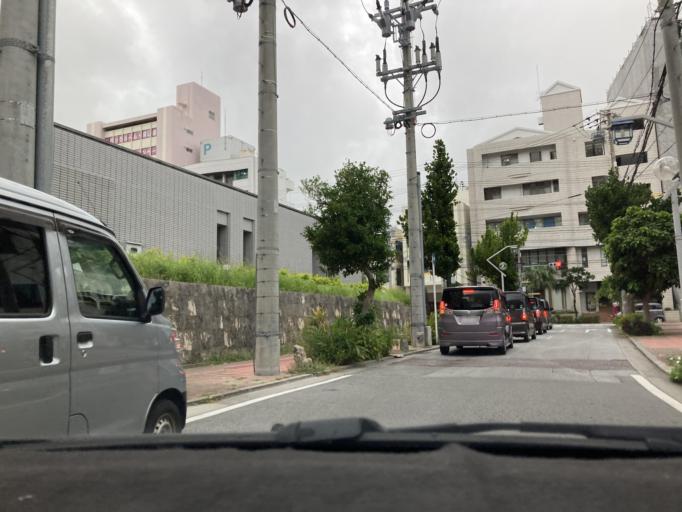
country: JP
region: Okinawa
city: Naha-shi
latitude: 26.2113
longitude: 127.6807
